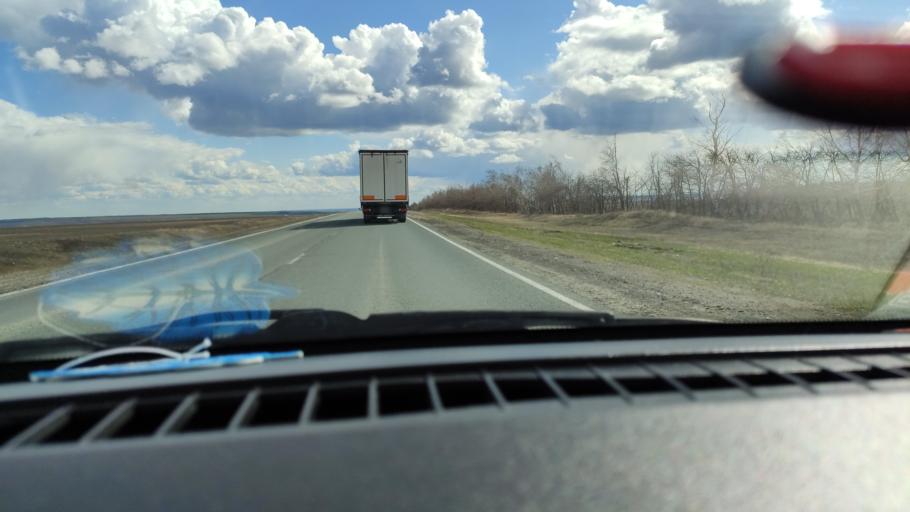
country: RU
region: Saratov
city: Dukhovnitskoye
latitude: 52.7870
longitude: 48.2330
